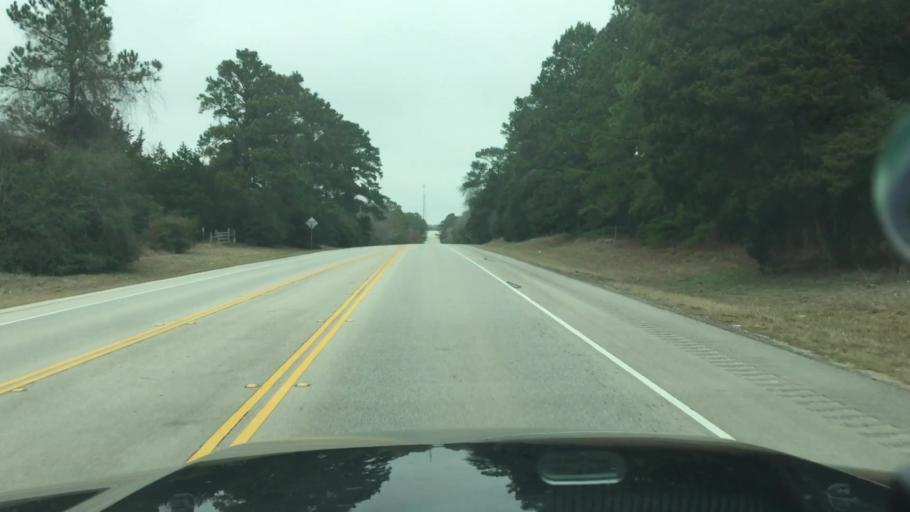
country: US
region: Texas
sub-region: Fayette County
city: La Grange
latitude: 30.0089
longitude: -96.8950
